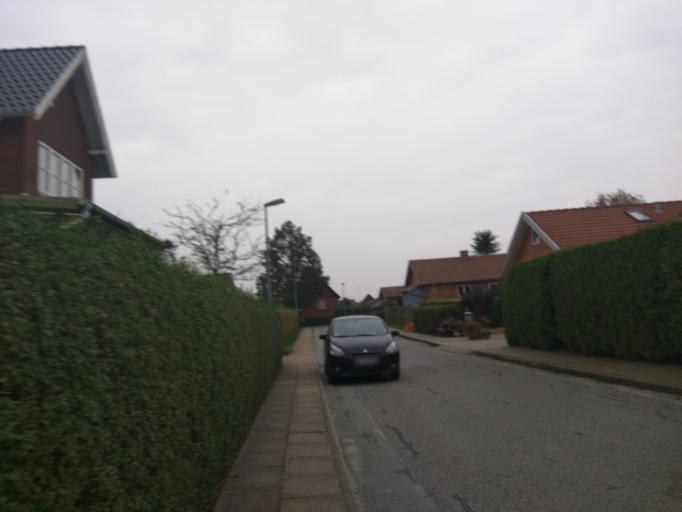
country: DK
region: Central Jutland
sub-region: Viborg Kommune
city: Viborg
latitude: 56.4587
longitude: 9.3854
